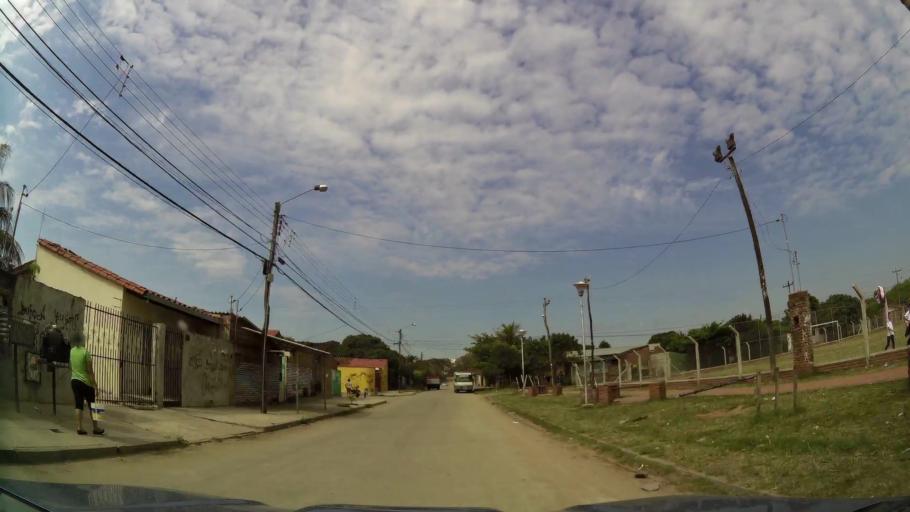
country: BO
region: Santa Cruz
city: Santa Cruz de la Sierra
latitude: -17.7292
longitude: -63.1806
